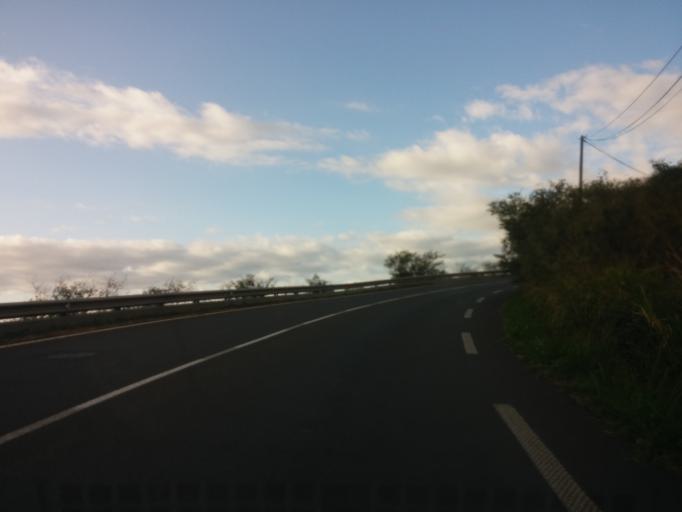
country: RE
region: Reunion
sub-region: Reunion
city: Saint-Paul
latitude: -21.0424
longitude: 55.2404
